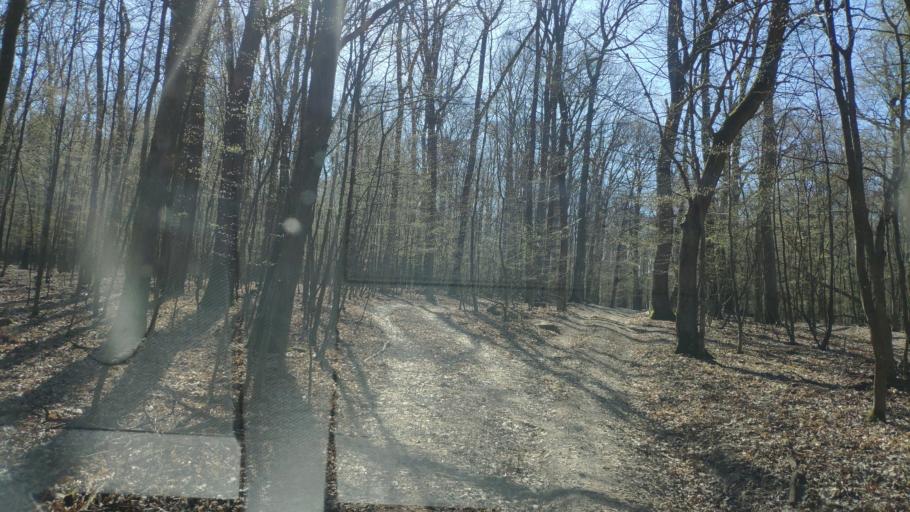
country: SK
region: Kosicky
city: Moldava nad Bodvou
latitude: 48.5656
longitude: 20.9339
